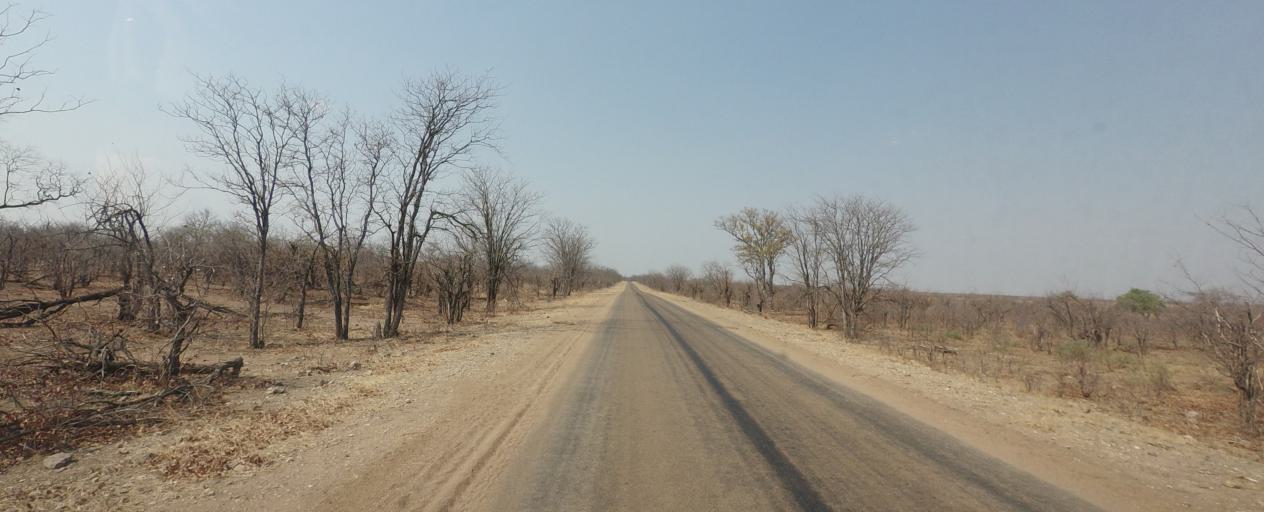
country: ZA
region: Limpopo
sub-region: Mopani District Municipality
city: Giyani
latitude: -23.1961
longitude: 31.3111
